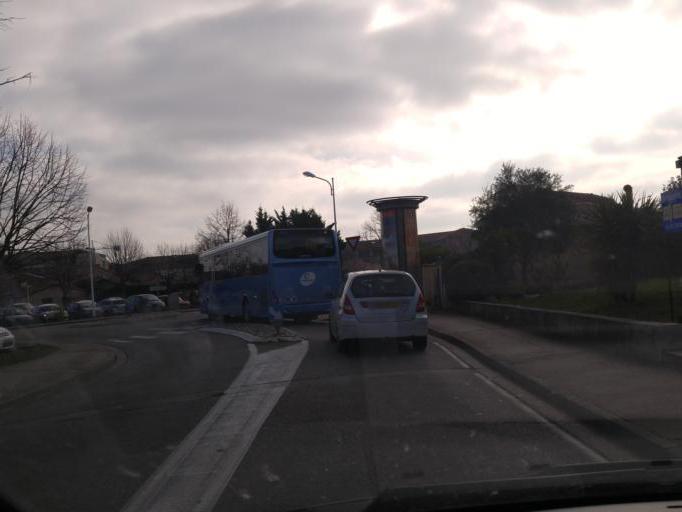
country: FR
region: Midi-Pyrenees
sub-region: Departement de la Haute-Garonne
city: Blagnac
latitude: 43.6418
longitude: 1.3755
